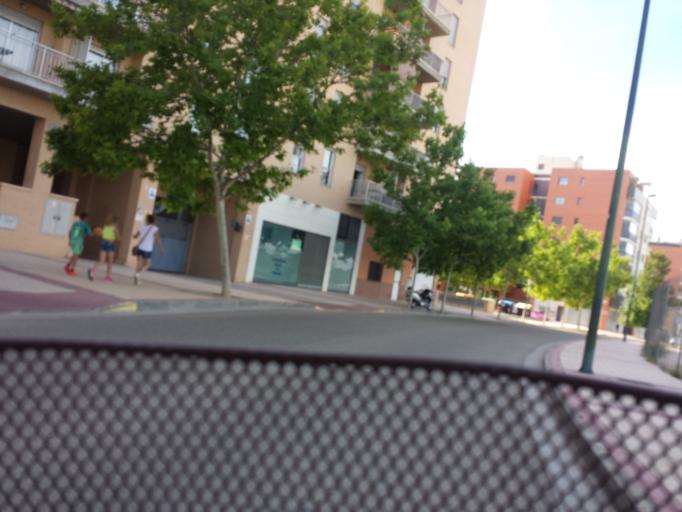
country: ES
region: Aragon
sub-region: Provincia de Zaragoza
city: Montecanal
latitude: 41.6357
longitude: -0.9444
